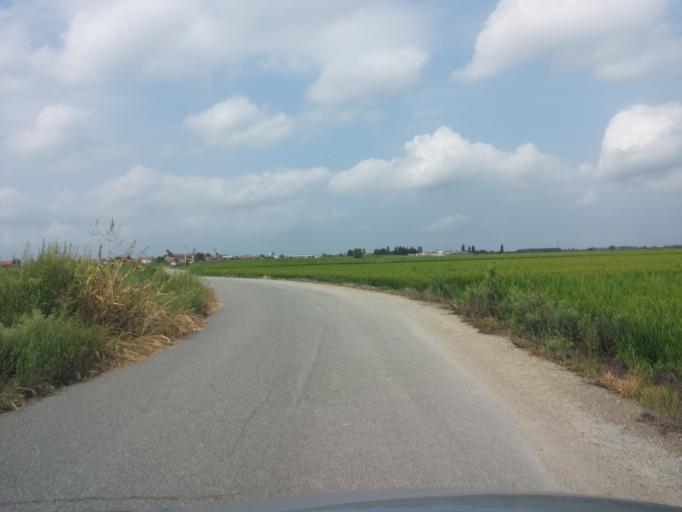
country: IT
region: Piedmont
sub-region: Provincia di Vercelli
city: Prarolo
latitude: 45.2829
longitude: 8.4905
